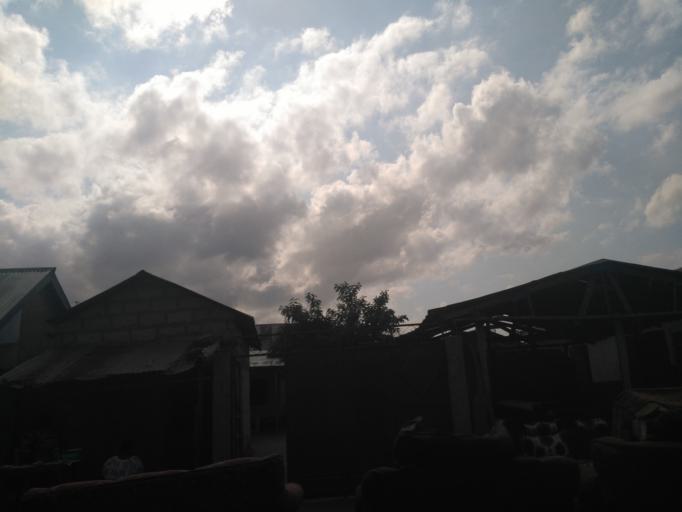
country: TZ
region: Dar es Salaam
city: Dar es Salaam
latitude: -6.8980
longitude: 39.2834
